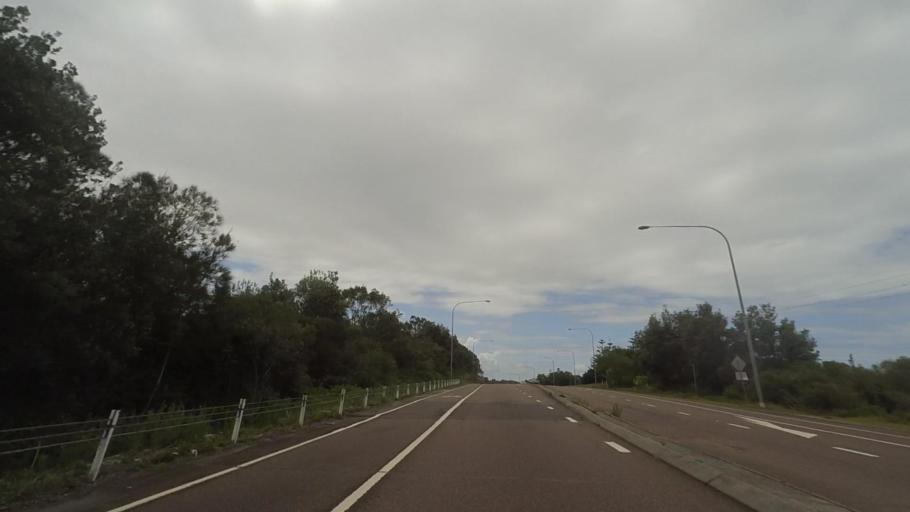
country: AU
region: New South Wales
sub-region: Wyong Shire
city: The Entrance
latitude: -33.3114
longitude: 151.5200
